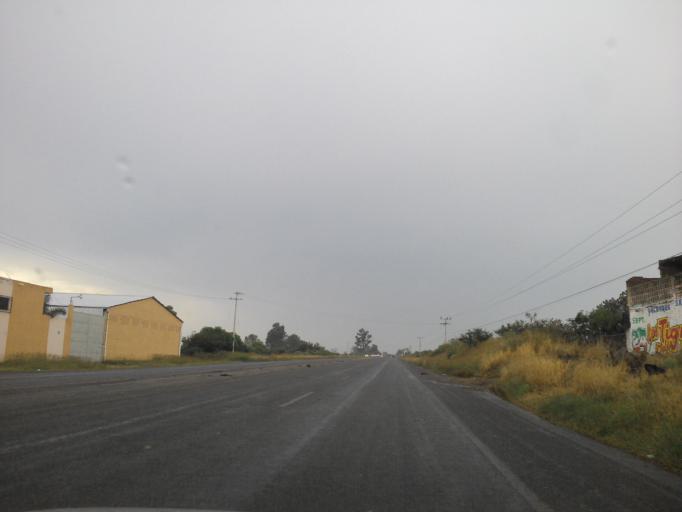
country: MX
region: Jalisco
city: Capilla de Guadalupe
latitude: 20.8642
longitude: -102.6442
